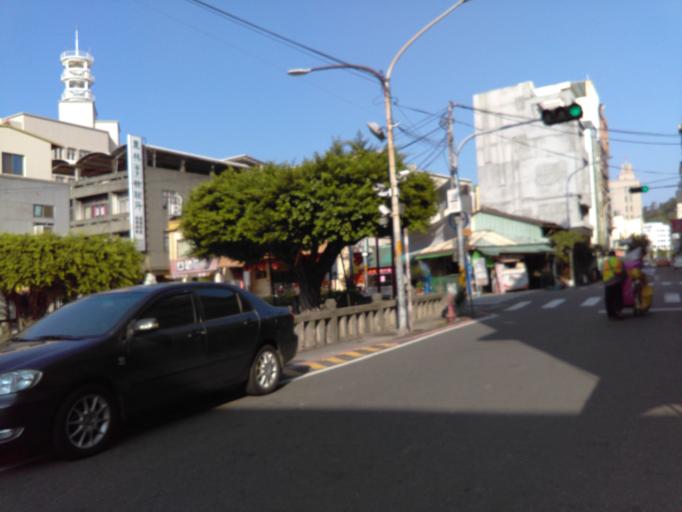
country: TW
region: Taiwan
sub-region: Changhua
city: Chang-hua
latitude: 24.0795
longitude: 120.5425
